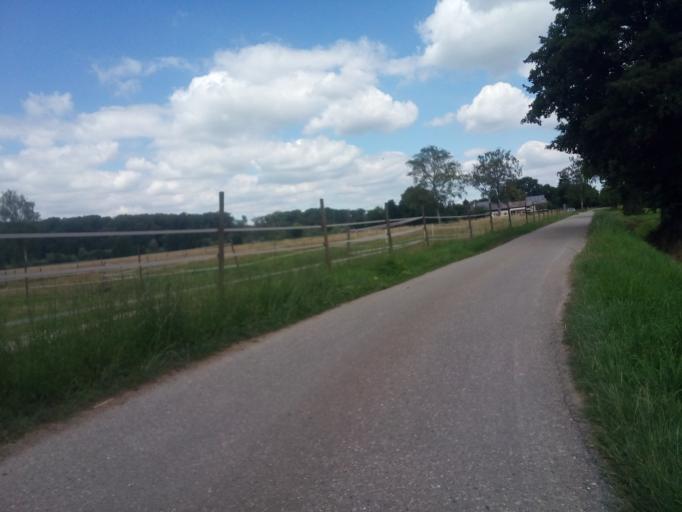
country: DE
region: Baden-Wuerttemberg
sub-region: Freiburg Region
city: Renchen
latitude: 48.6227
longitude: 7.9736
